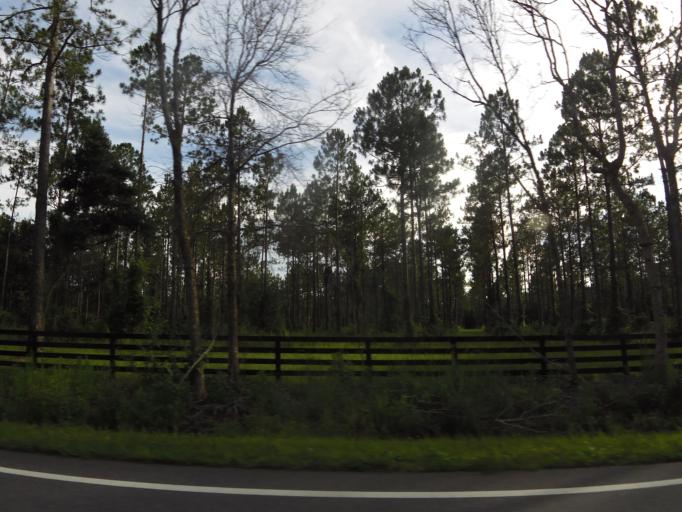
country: US
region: Florida
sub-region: Clay County
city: Green Cove Springs
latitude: 30.0005
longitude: -81.5444
